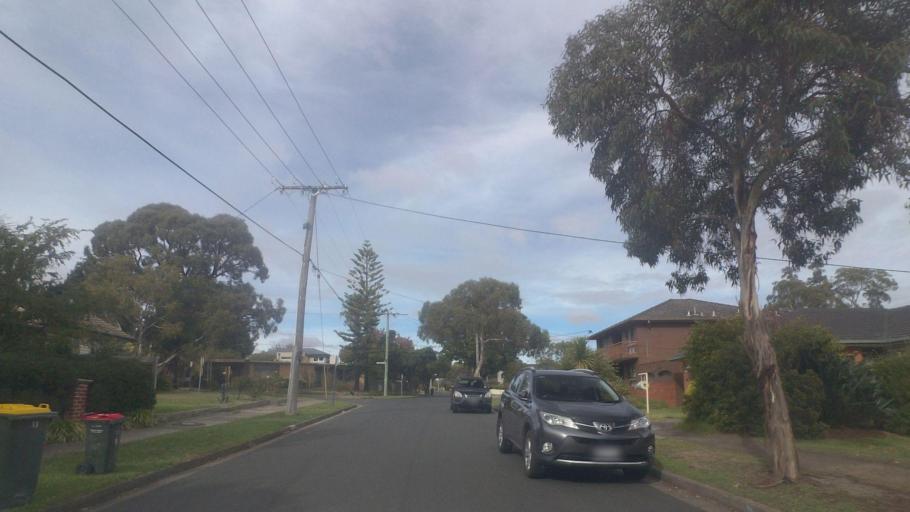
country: AU
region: Victoria
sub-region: Whitehorse
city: Blackburn South
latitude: -37.8331
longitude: 145.1465
